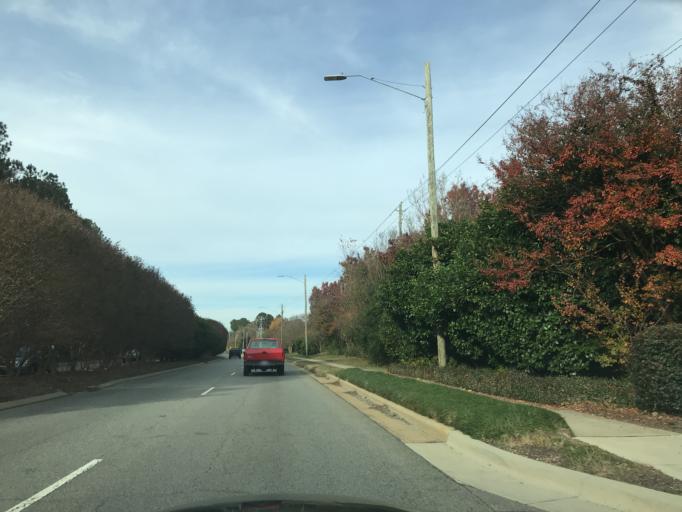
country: US
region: North Carolina
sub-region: Wake County
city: West Raleigh
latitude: 35.8787
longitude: -78.6788
